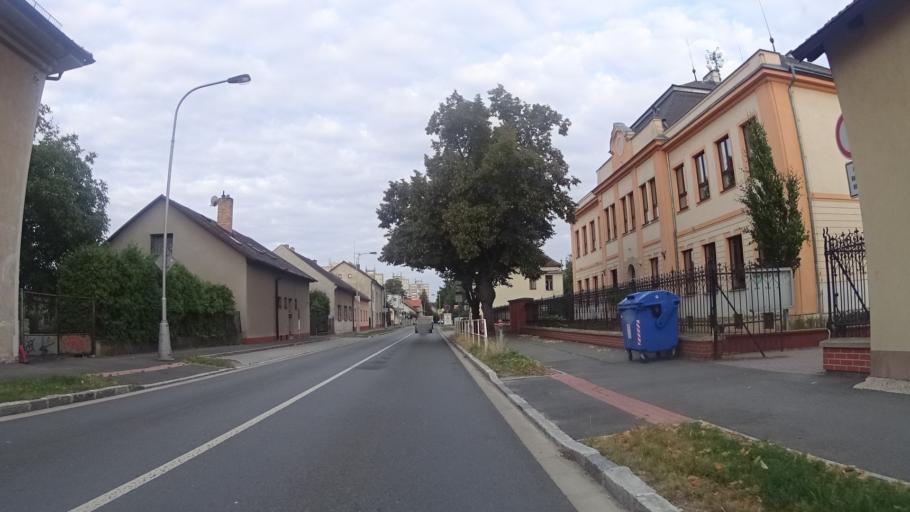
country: CZ
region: Kralovehradecky
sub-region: Okres Hradec Kralove
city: Hradec Kralove
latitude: 50.2042
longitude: 15.8547
